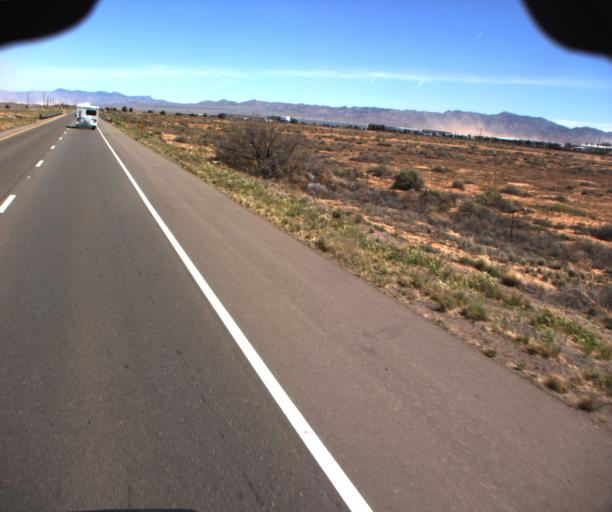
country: US
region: Arizona
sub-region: Mohave County
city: New Kingman-Butler
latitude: 35.2646
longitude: -113.9650
